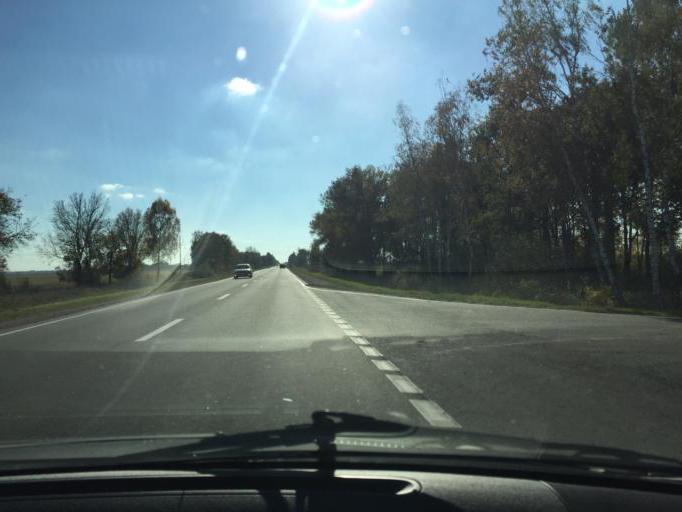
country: BY
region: Minsk
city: Salihorsk
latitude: 52.9091
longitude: 27.4789
